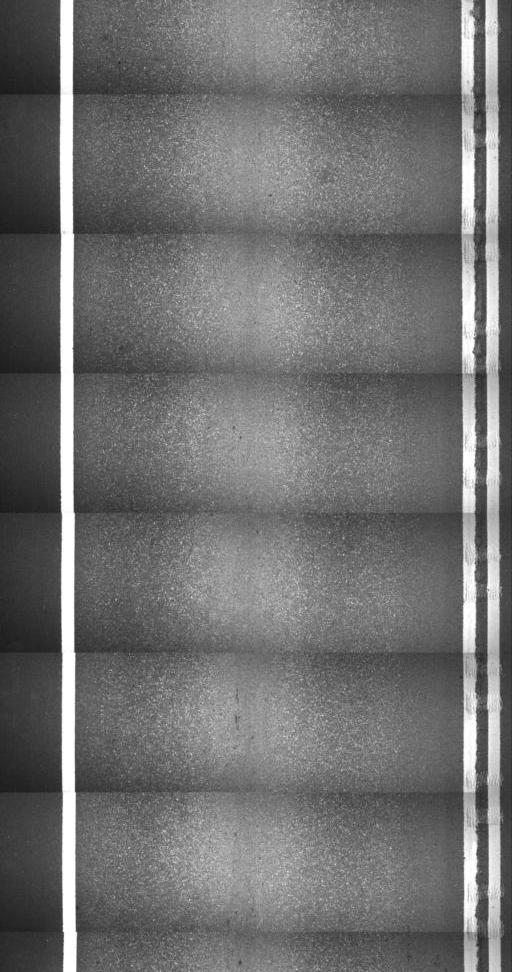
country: US
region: Vermont
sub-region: Washington County
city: Waterbury
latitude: 44.2864
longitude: -72.7806
